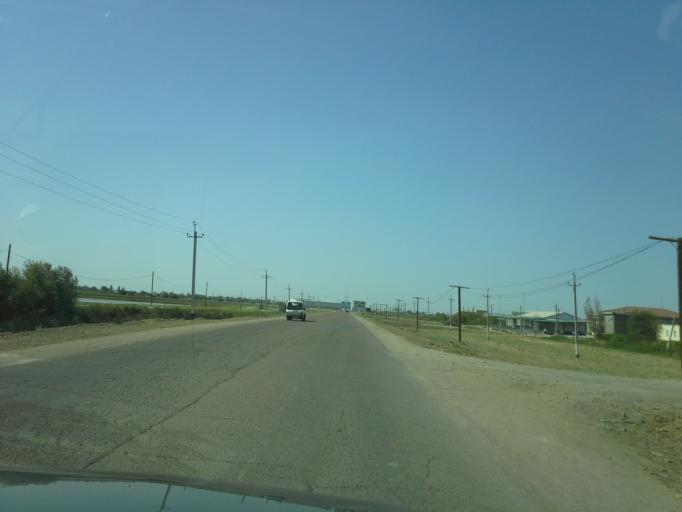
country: TM
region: Dasoguz
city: Dasoguz
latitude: 41.8056
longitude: 60.0091
